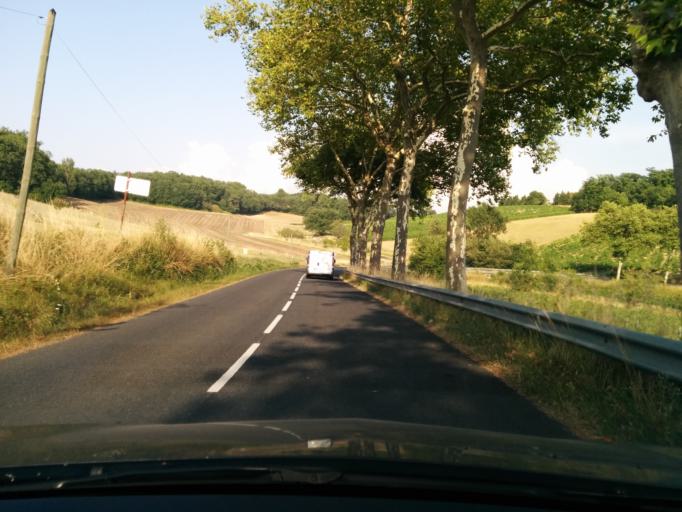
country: FR
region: Midi-Pyrenees
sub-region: Departement du Tarn
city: Cahuzac-sur-Vere
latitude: 43.9475
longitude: 1.9112
